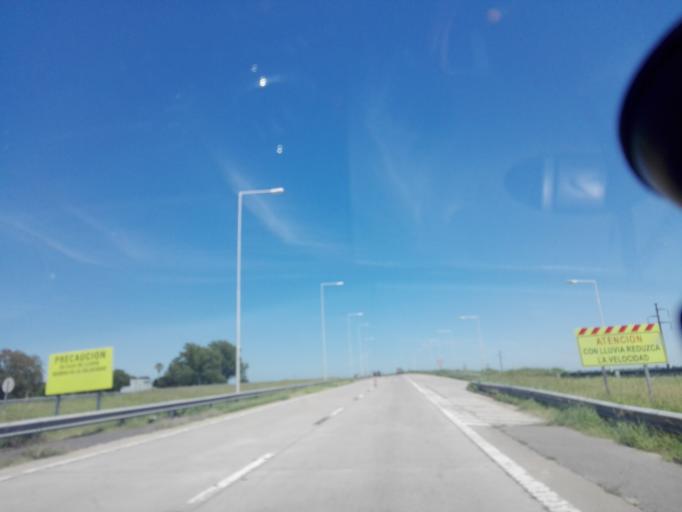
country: AR
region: Santa Fe
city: Canada de Gomez
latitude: -32.8547
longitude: -61.3420
